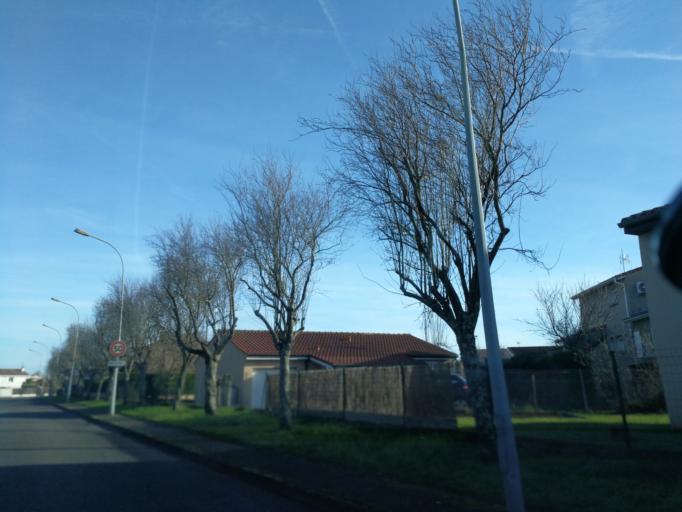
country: FR
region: Midi-Pyrenees
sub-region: Departement de la Haute-Garonne
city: L'Union
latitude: 43.6473
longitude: 1.4738
